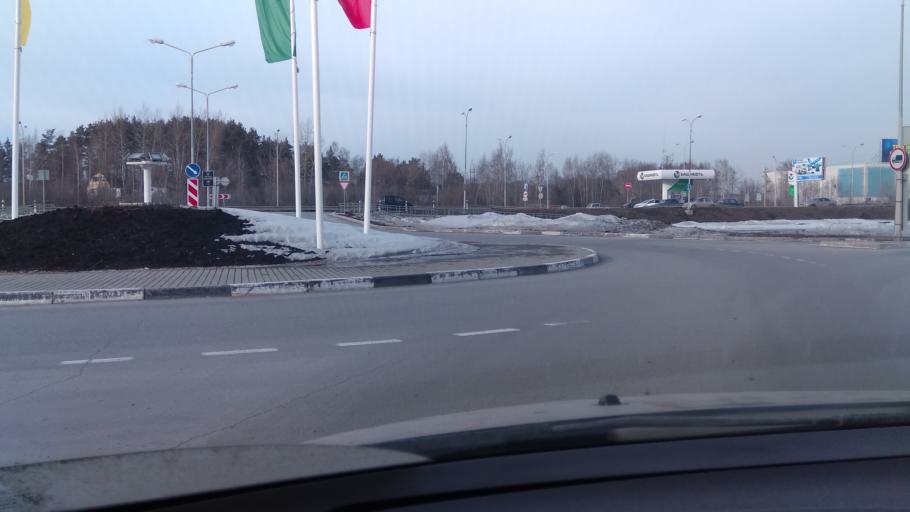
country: RU
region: Sverdlovsk
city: Shirokaya Rechka
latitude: 56.8251
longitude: 60.5045
